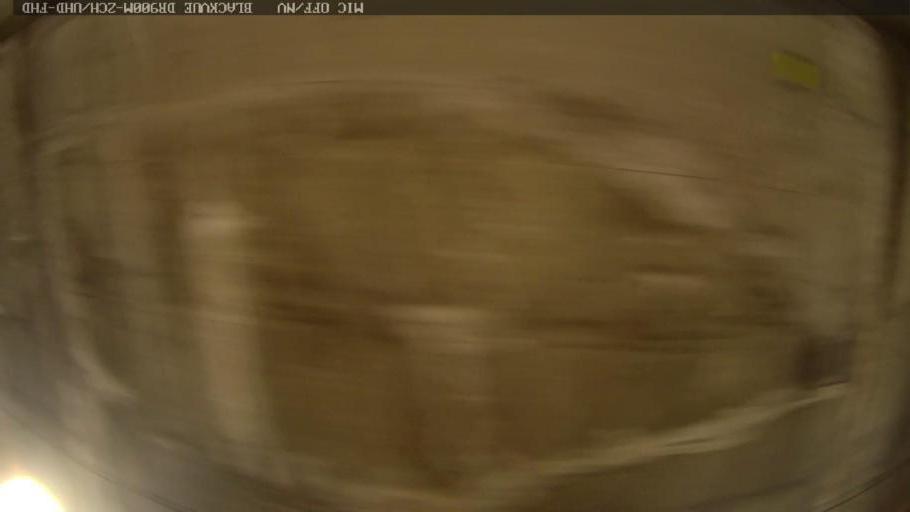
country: BR
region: Sao Paulo
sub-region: Cubatao
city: Cubatao
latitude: -23.8829
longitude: -46.4923
